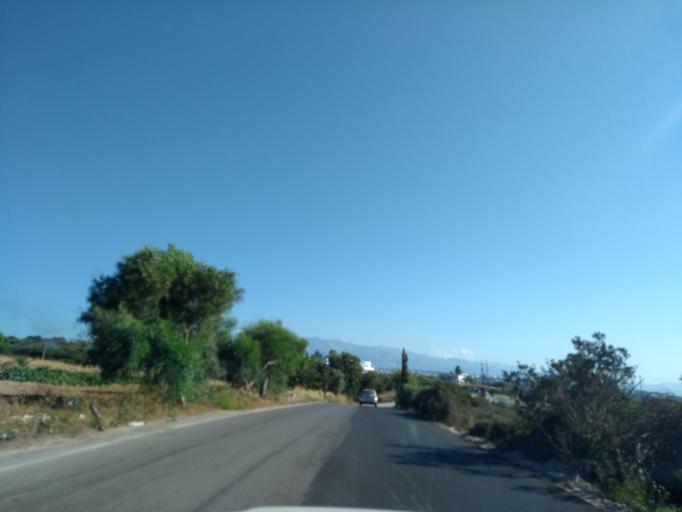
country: GR
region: Crete
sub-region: Nomos Chanias
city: Pithari
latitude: 35.5596
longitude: 24.0904
